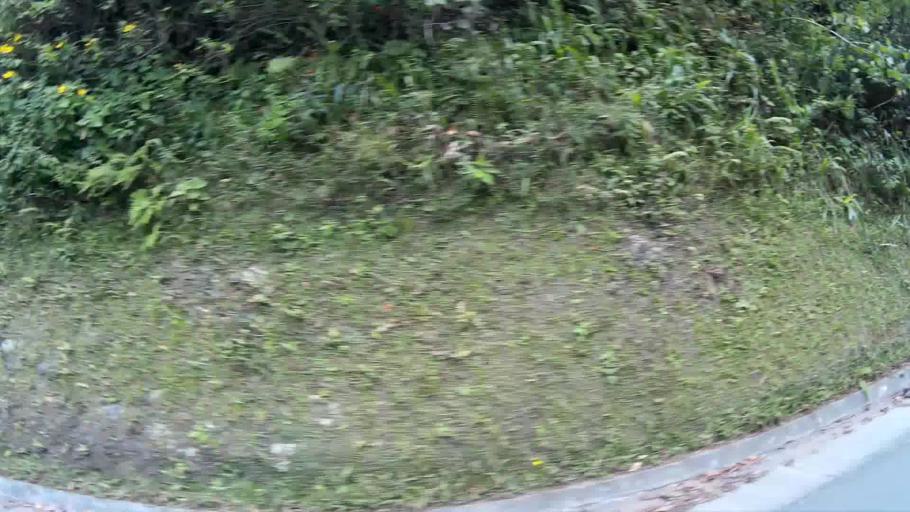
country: CO
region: Quindio
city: Circasia
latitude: 4.6010
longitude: -75.6369
